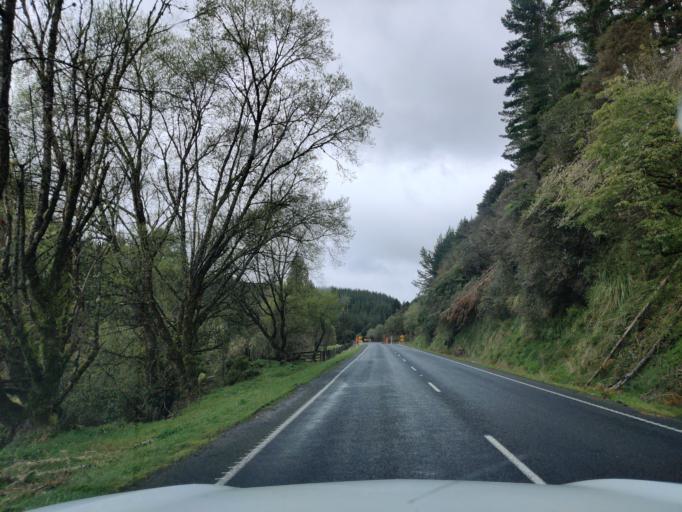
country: NZ
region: Waikato
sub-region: Otorohanga District
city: Otorohanga
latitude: -38.6548
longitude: 175.2081
